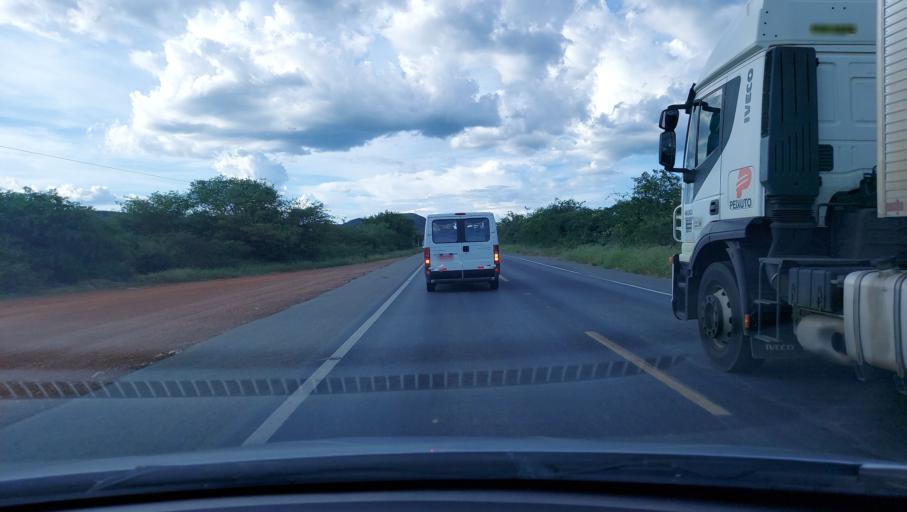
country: BR
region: Bahia
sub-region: Oliveira Dos Brejinhos
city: Beira Rio
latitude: -12.4289
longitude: -42.3490
